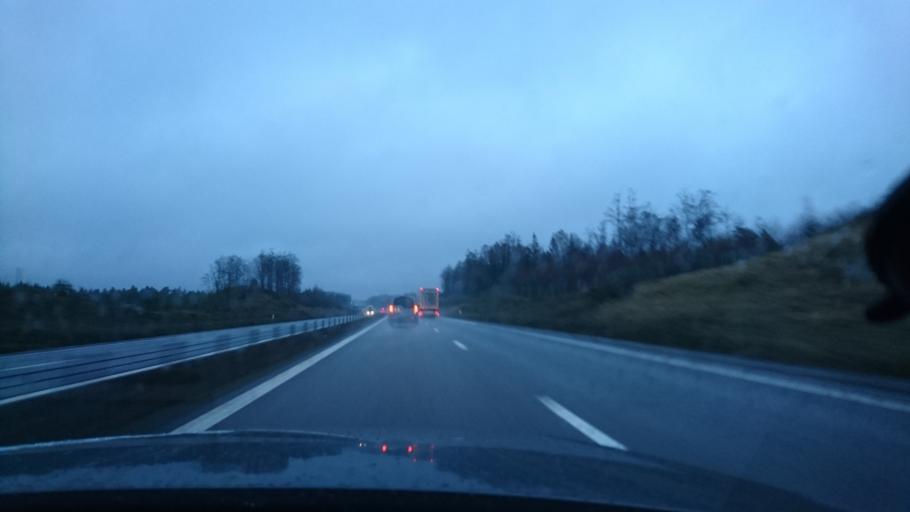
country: SE
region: Skane
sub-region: Orkelljunga Kommun
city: OErkelljunga
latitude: 56.3362
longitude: 13.4558
